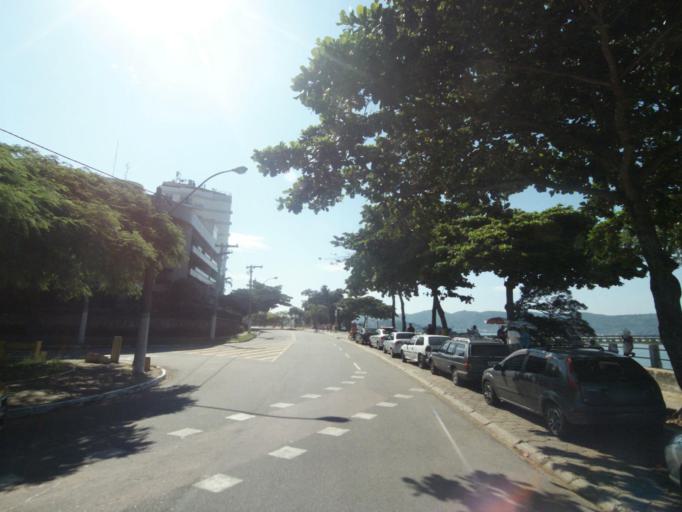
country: BR
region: Rio de Janeiro
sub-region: Niteroi
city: Niteroi
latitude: -22.9082
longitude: -43.1311
